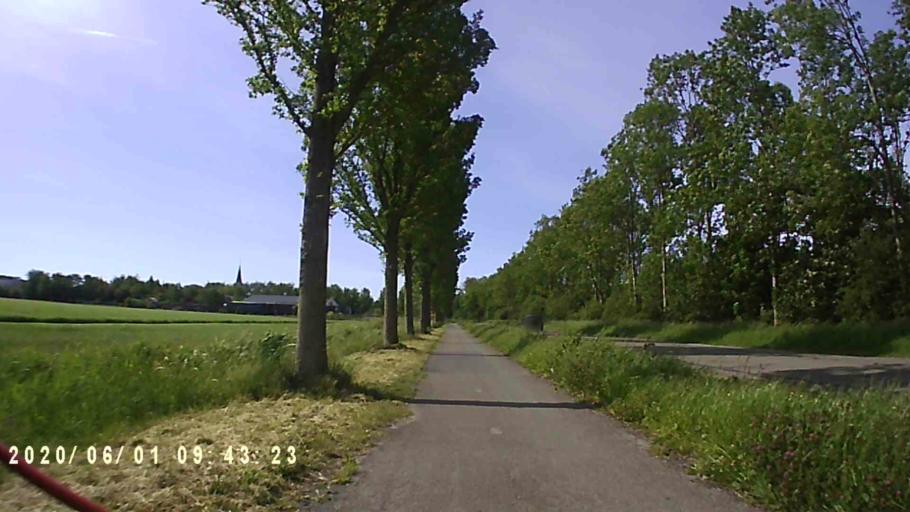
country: NL
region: Friesland
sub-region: Menameradiel
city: Menaam
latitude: 53.2410
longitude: 5.6836
